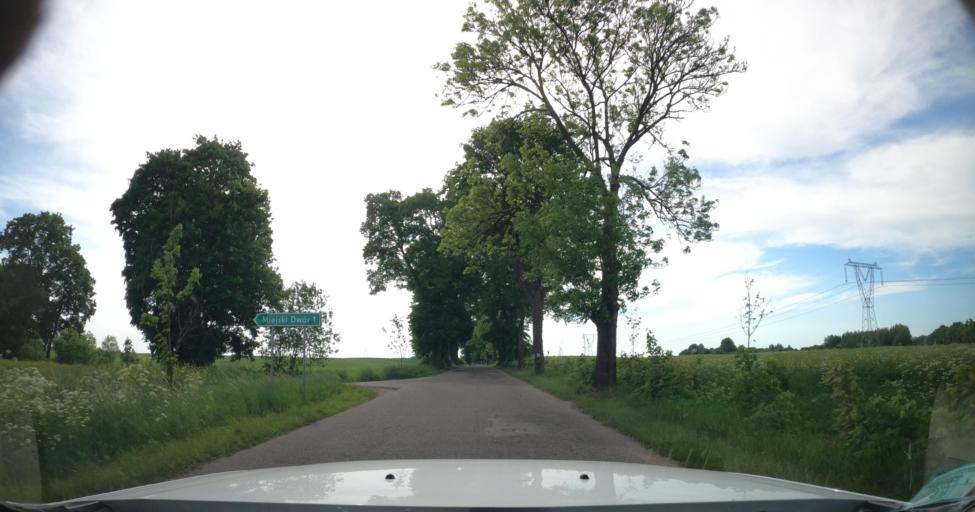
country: PL
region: Warmian-Masurian Voivodeship
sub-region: Powiat ostrodzki
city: Milakowo
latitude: 54.0179
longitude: 20.0481
